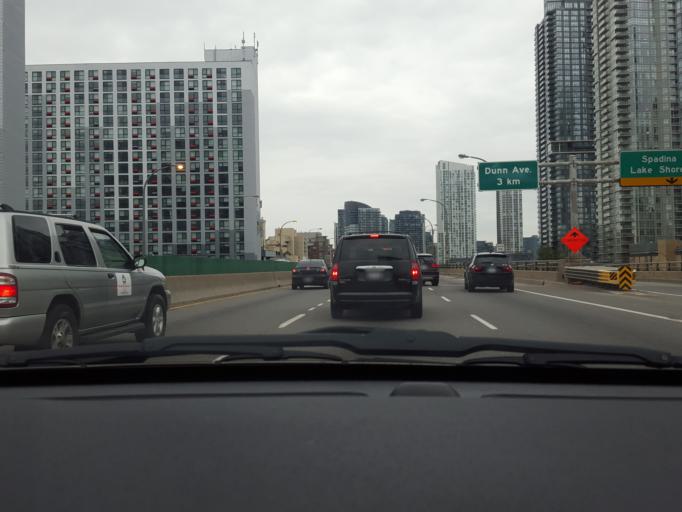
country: CA
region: Ontario
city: Toronto
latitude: 43.6394
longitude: -79.3886
